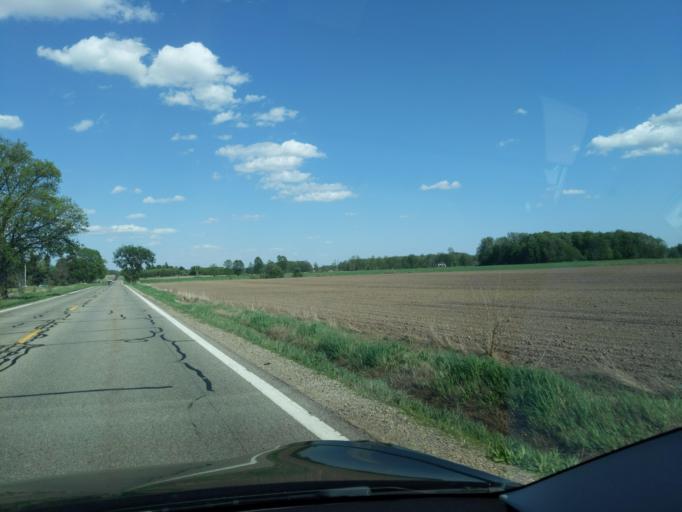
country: US
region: Michigan
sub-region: Kent County
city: Lowell
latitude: 42.7988
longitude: -85.3160
